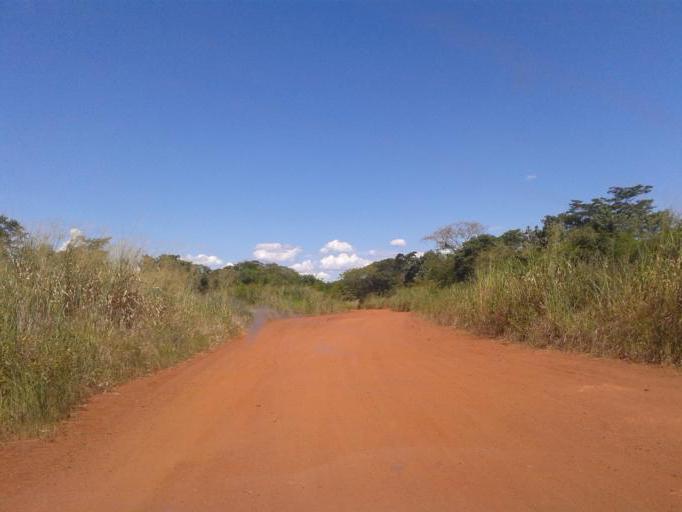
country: BR
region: Minas Gerais
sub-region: Capinopolis
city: Capinopolis
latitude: -18.6106
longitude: -49.5949
